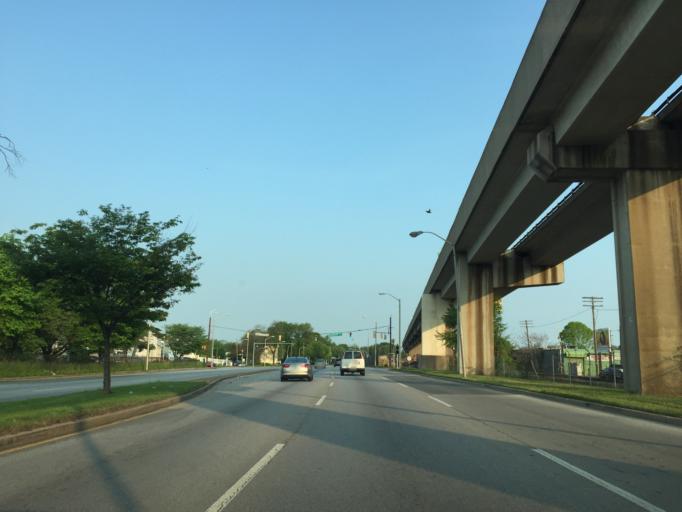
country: US
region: Maryland
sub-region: Baltimore County
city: Lochearn
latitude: 39.3415
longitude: -76.6837
